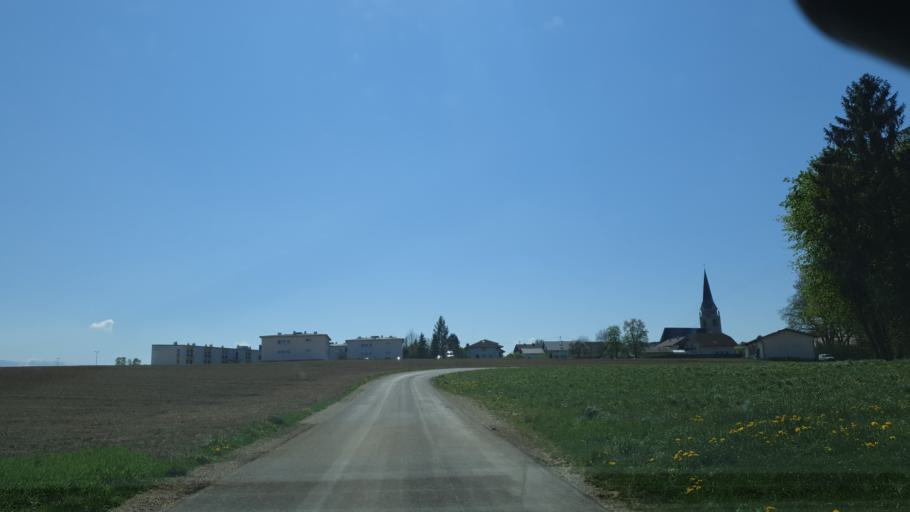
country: AT
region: Upper Austria
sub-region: Politischer Bezirk Vocklabruck
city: Gampern
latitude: 47.9925
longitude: 13.5586
